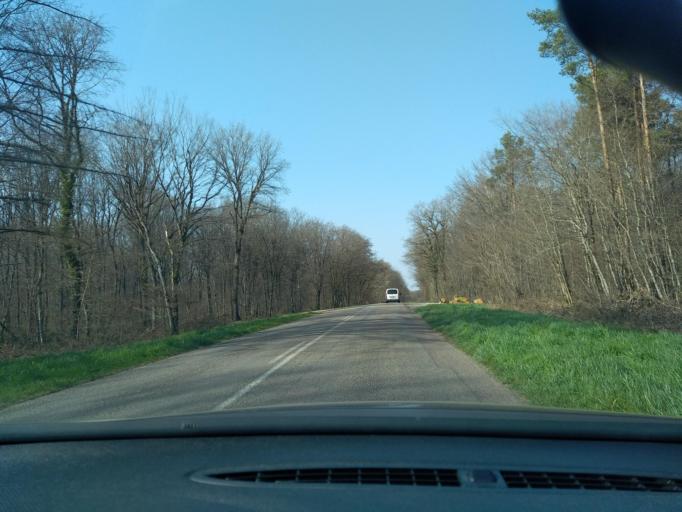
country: FR
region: Franche-Comte
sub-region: Departement du Jura
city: Dole
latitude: 47.0518
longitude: 5.5152
